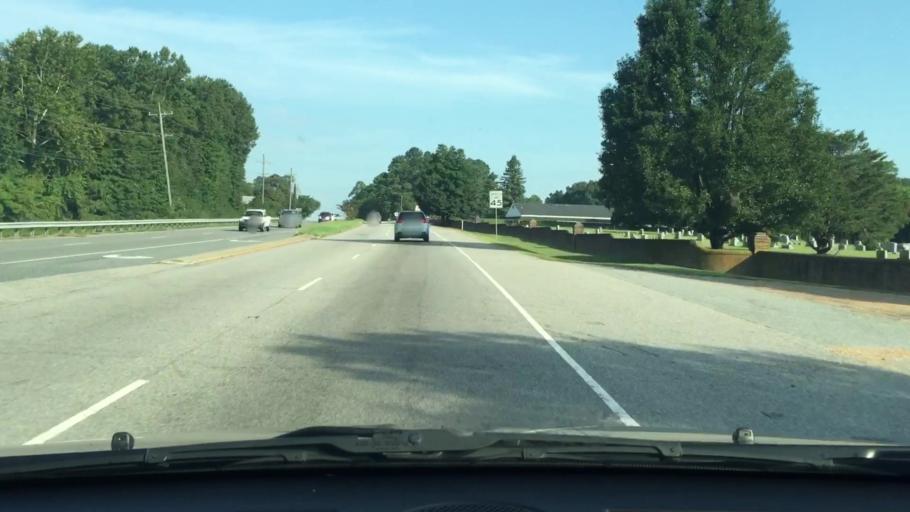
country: US
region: Virginia
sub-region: Isle of Wight County
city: Carrollton
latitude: 36.9404
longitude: -76.5880
